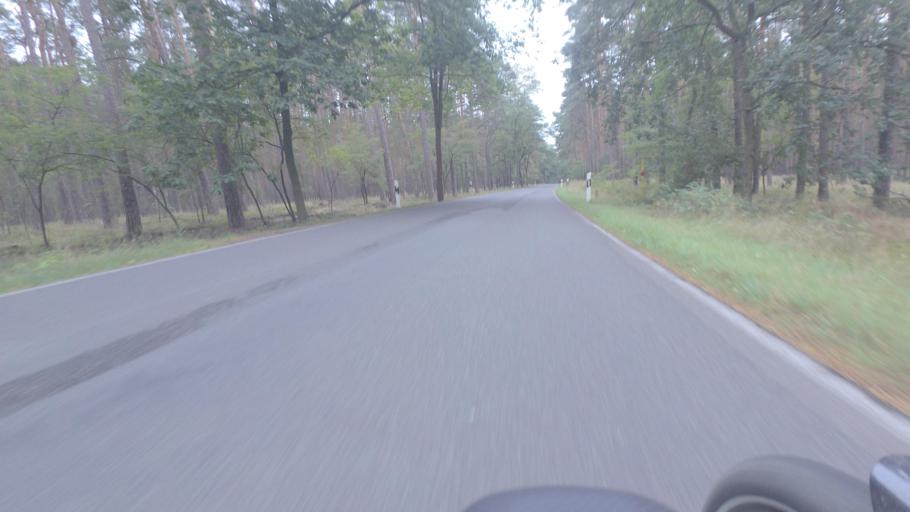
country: DE
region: Brandenburg
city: Luckenwalde
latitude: 52.1331
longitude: 13.1901
